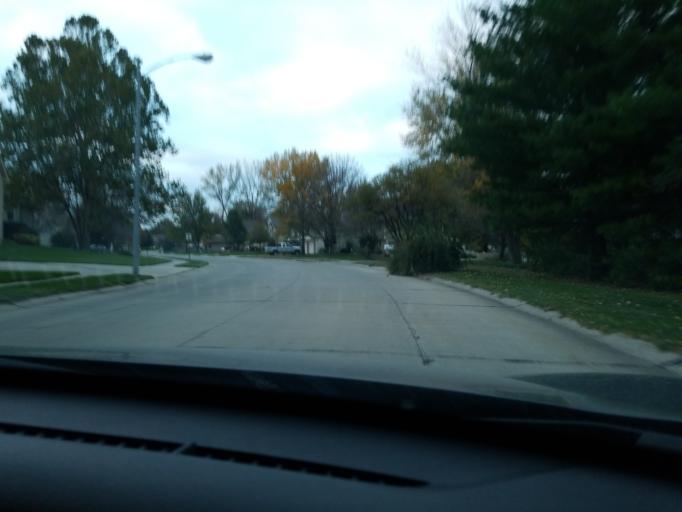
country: US
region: Nebraska
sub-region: Sarpy County
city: La Vista
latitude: 41.1703
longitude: -96.0286
